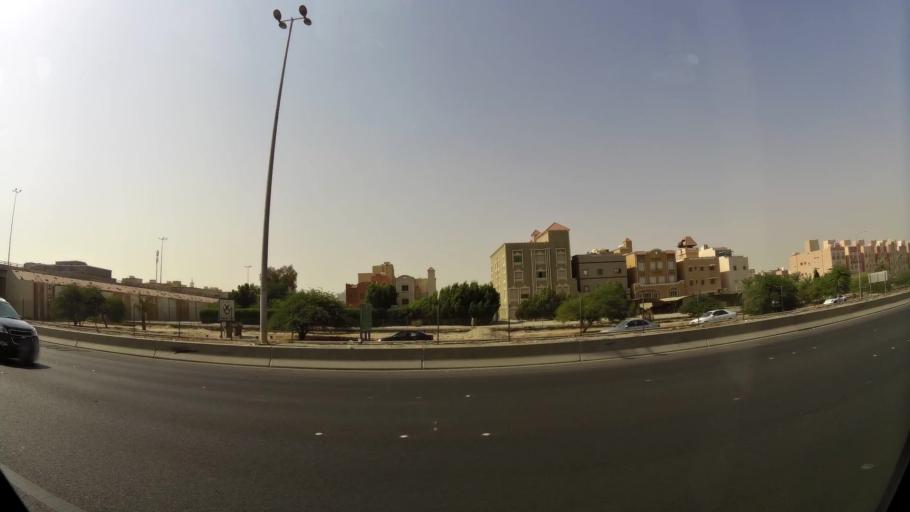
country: KW
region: Al Ahmadi
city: Al Fintas
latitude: 29.1799
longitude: 48.1133
